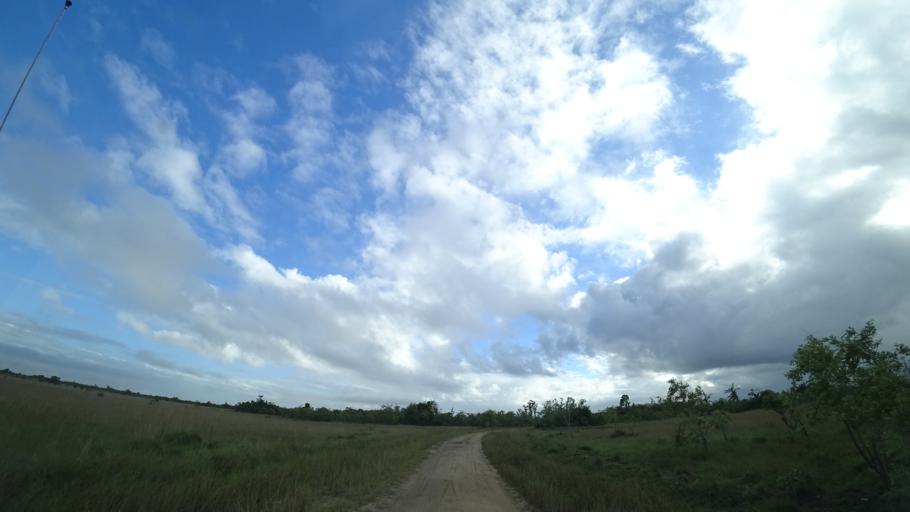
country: MZ
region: Sofala
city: Beira
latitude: -19.6678
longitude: 35.0583
